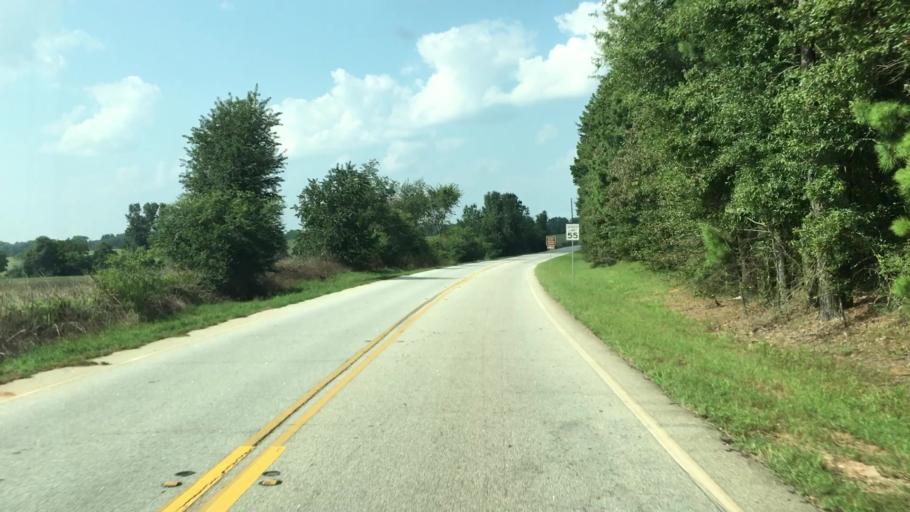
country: US
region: Georgia
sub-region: Newton County
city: Covington
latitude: 33.4674
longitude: -83.7536
